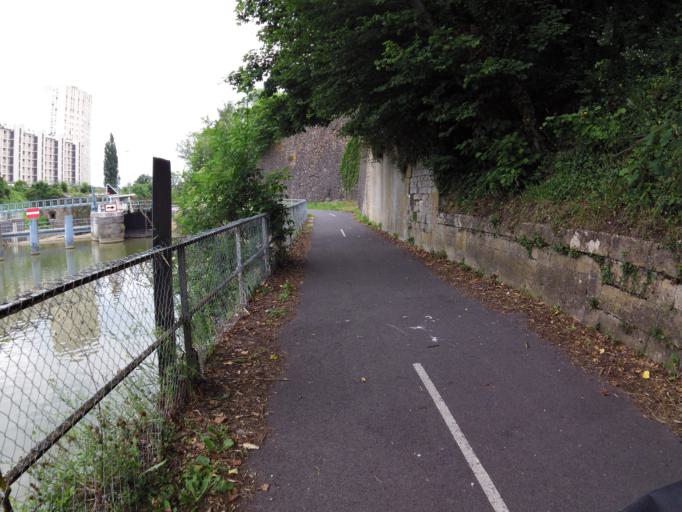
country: FR
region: Champagne-Ardenne
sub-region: Departement des Ardennes
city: Charleville-Mezieres
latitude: 49.7603
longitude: 4.7248
